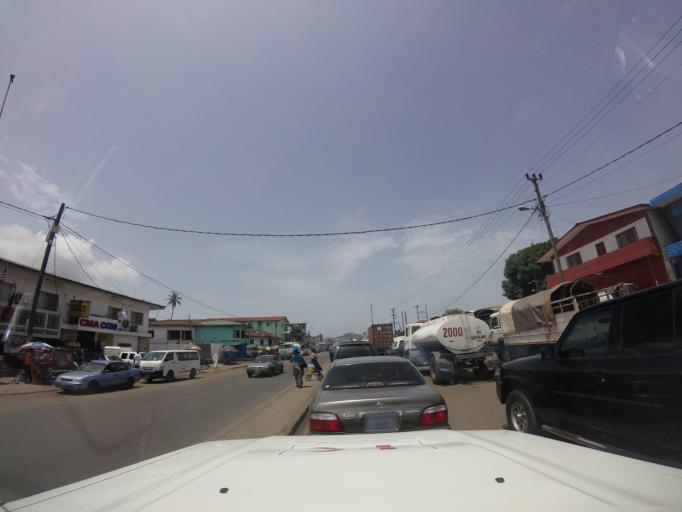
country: LR
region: Montserrado
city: Monrovia
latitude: 6.3350
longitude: -10.7958
